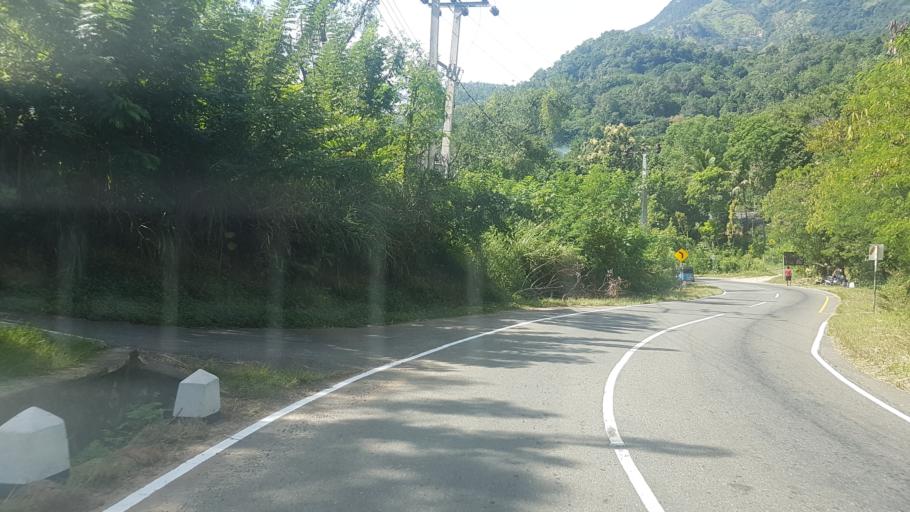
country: LK
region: Uva
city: Haputale
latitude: 6.8143
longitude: 81.0828
